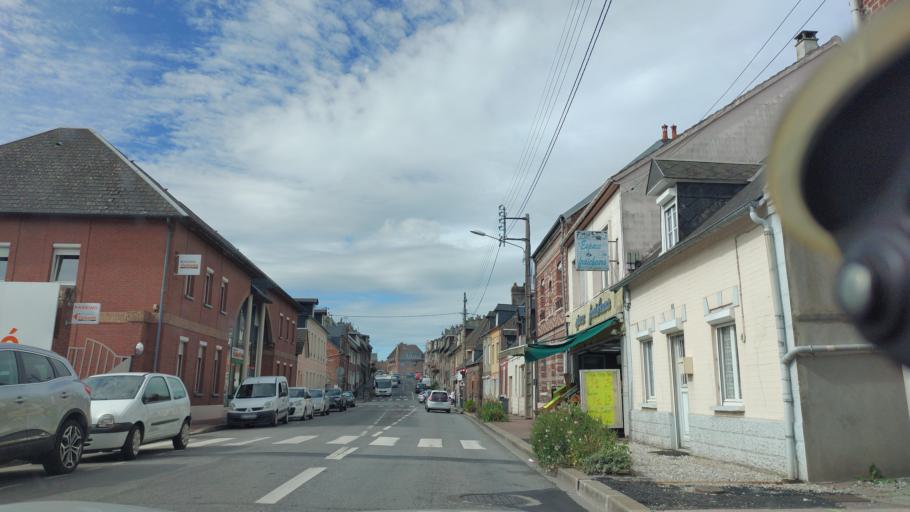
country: FR
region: Haute-Normandie
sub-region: Departement de la Seine-Maritime
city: Eu
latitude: 50.0548
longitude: 1.4230
